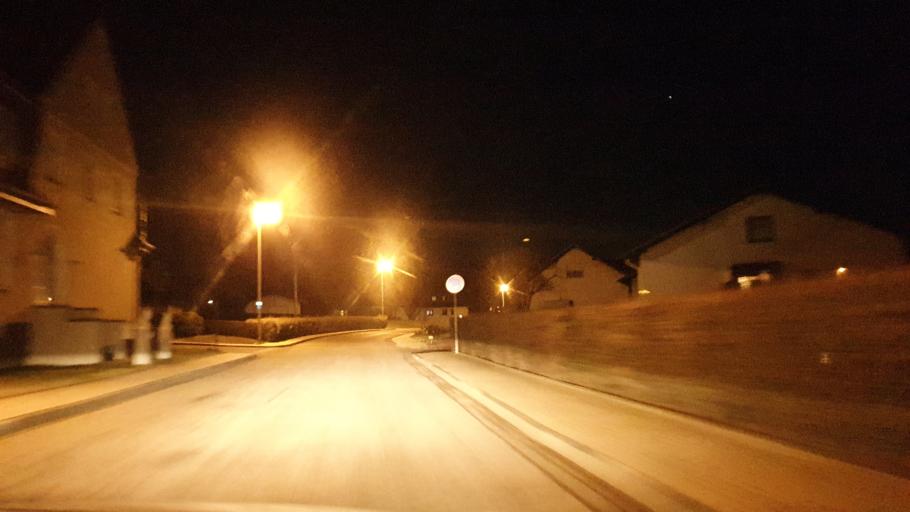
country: DE
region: Rheinland-Pfalz
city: Oberdreis
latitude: 50.6398
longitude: 7.6471
